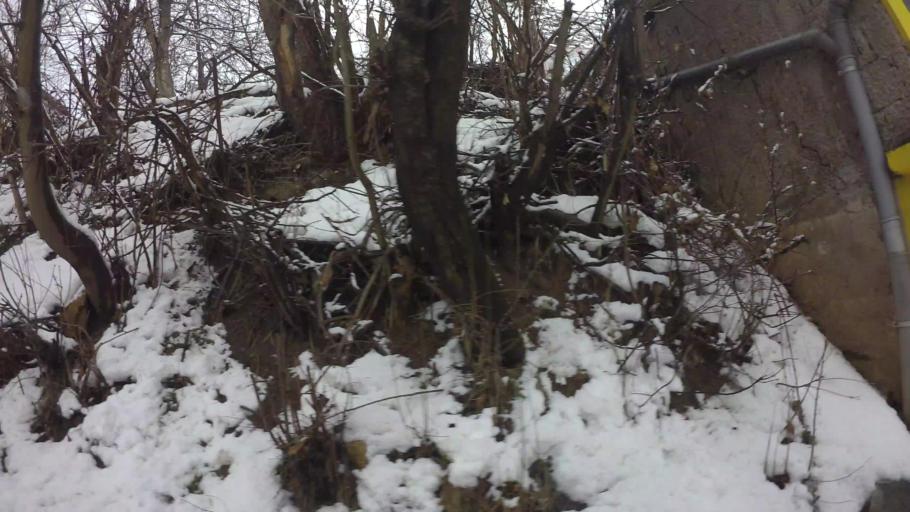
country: BA
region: Federation of Bosnia and Herzegovina
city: Kobilja Glava
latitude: 43.8507
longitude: 18.4297
